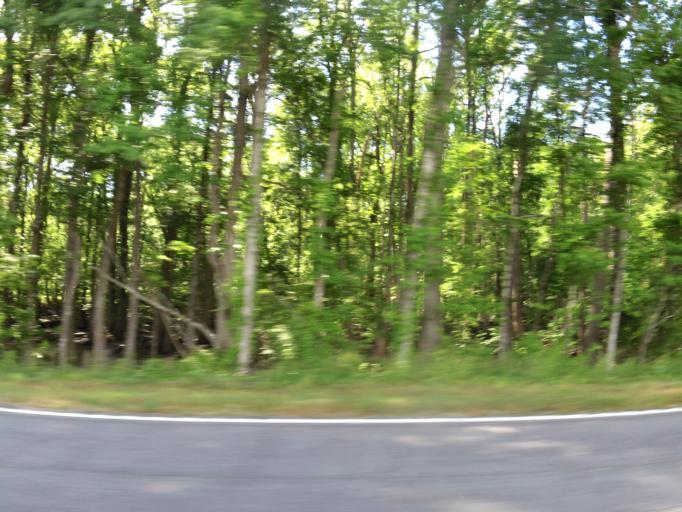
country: US
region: South Carolina
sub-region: Allendale County
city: Allendale
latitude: 33.1109
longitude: -81.1872
